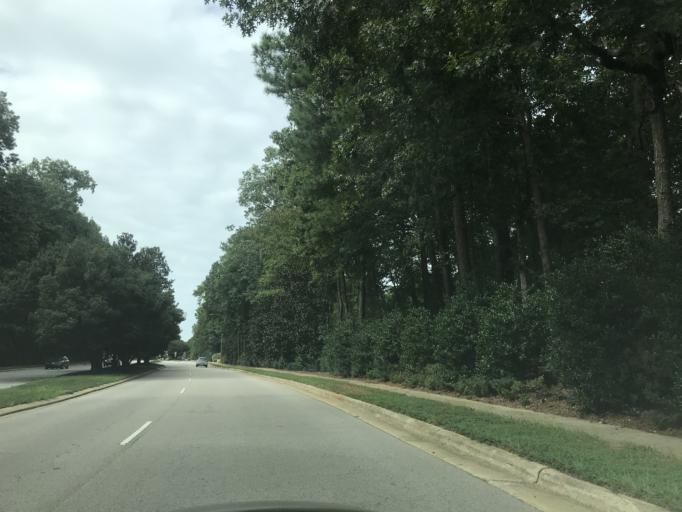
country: US
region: North Carolina
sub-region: Wake County
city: Cary
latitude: 35.7314
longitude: -78.7770
